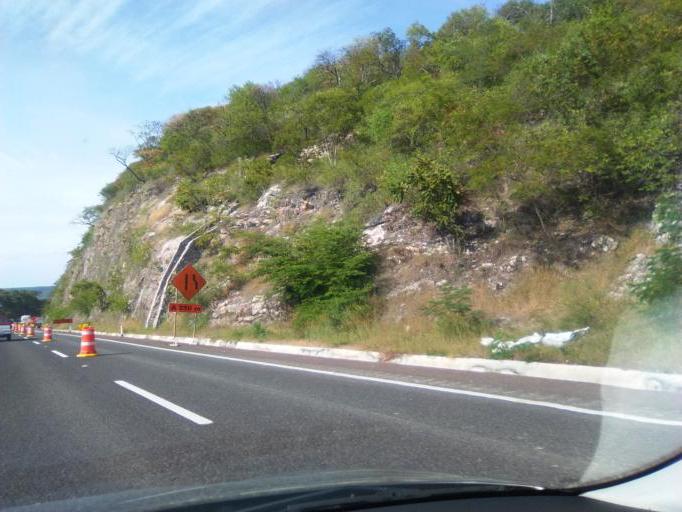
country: MX
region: Morelos
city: Tilzapotla
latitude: 18.4012
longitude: -99.1713
